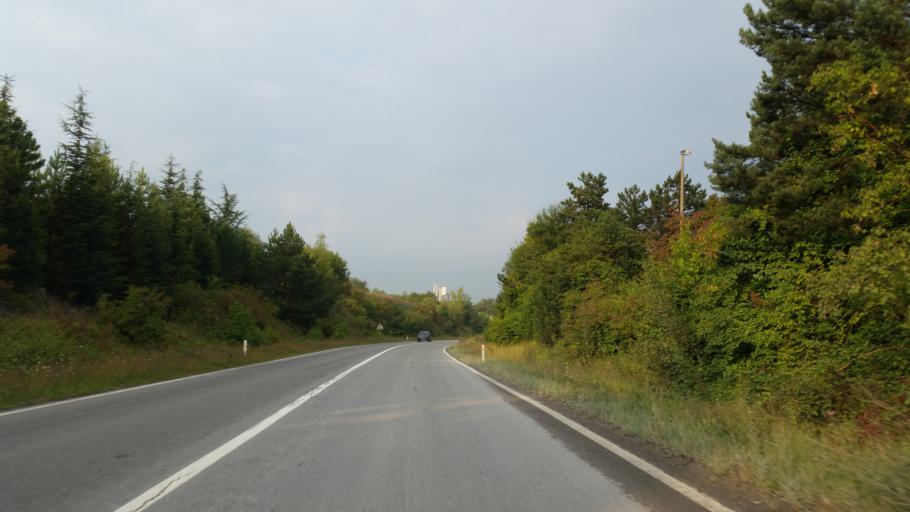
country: BE
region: Wallonia
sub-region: Province de Namur
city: Rochefort
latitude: 50.1669
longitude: 5.2624
